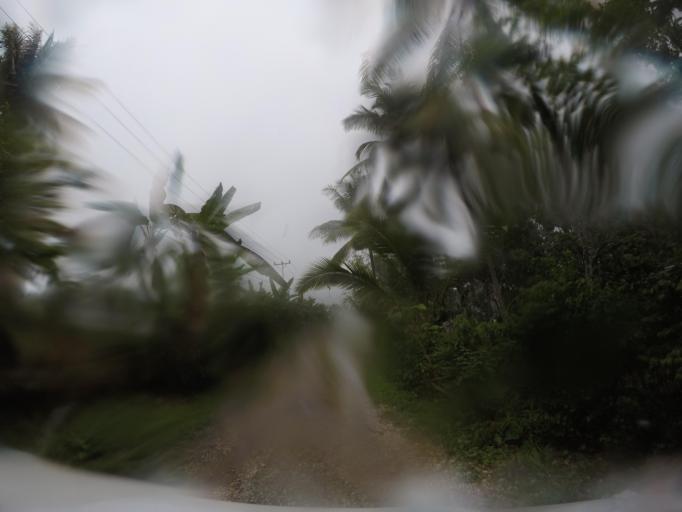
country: TL
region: Baucau
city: Venilale
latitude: -8.6340
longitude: 126.4411
